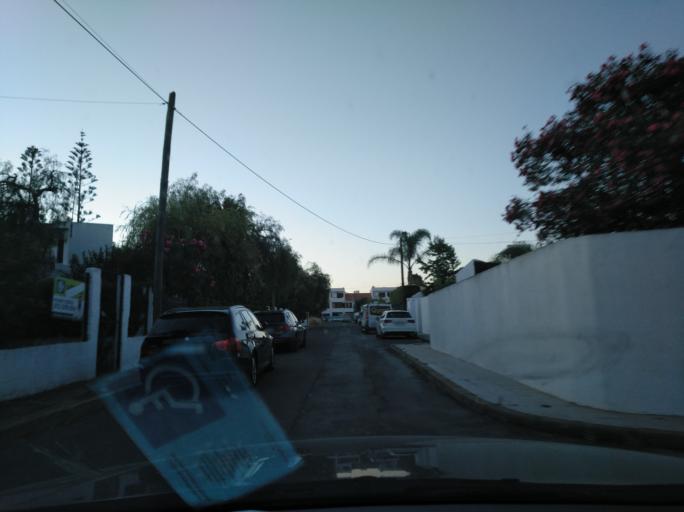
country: PT
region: Faro
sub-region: Tavira
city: Tavira
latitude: 37.1395
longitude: -7.5977
